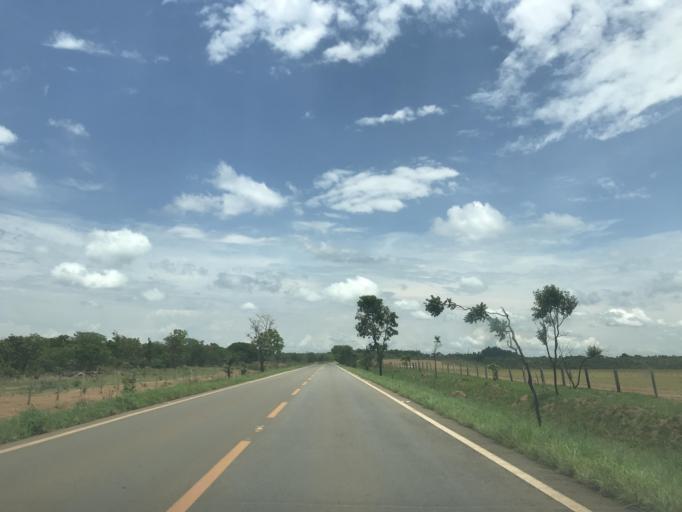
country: BR
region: Goias
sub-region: Luziania
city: Luziania
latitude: -16.3969
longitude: -48.1351
